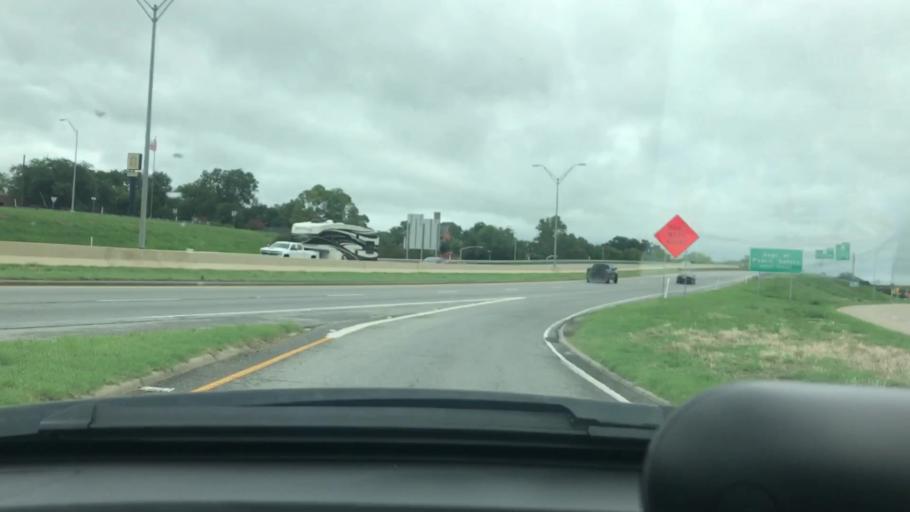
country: US
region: Texas
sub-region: Grayson County
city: Sherman
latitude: 33.6379
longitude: -96.6162
